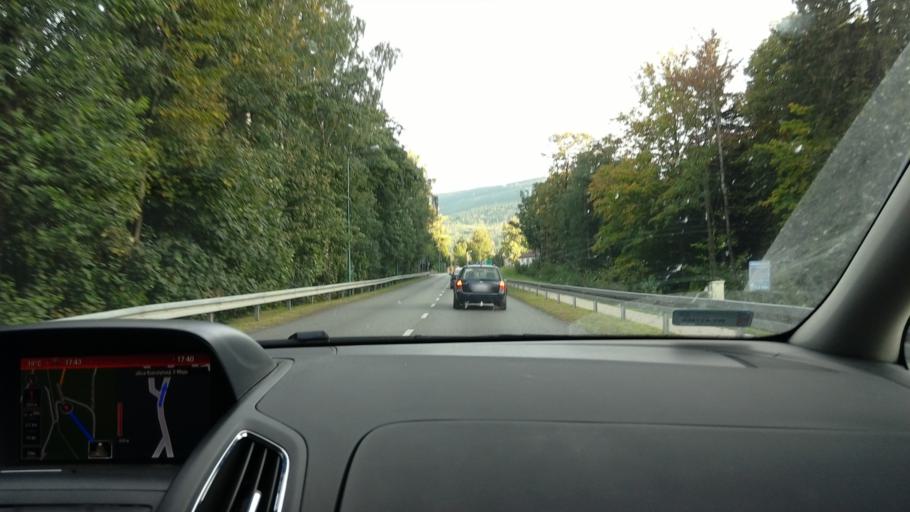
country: PL
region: Lower Silesian Voivodeship
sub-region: Powiat jeleniogorski
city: Karpacz
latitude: 50.7864
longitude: 15.7601
